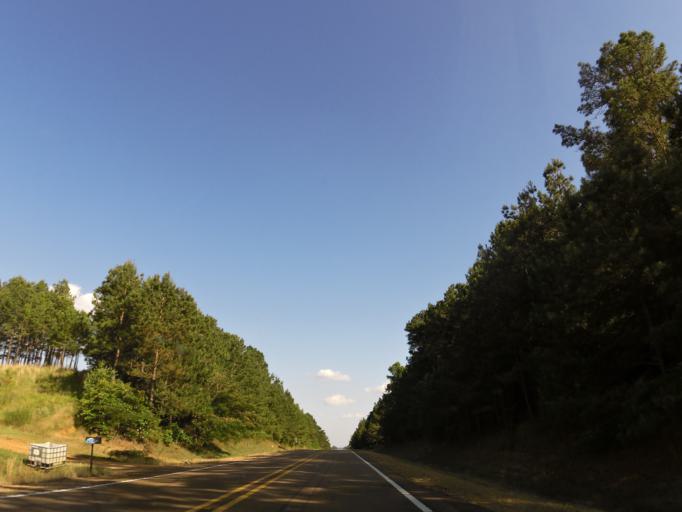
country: US
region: Mississippi
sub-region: Yalobusha County
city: Water Valley
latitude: 34.2118
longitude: -89.4858
